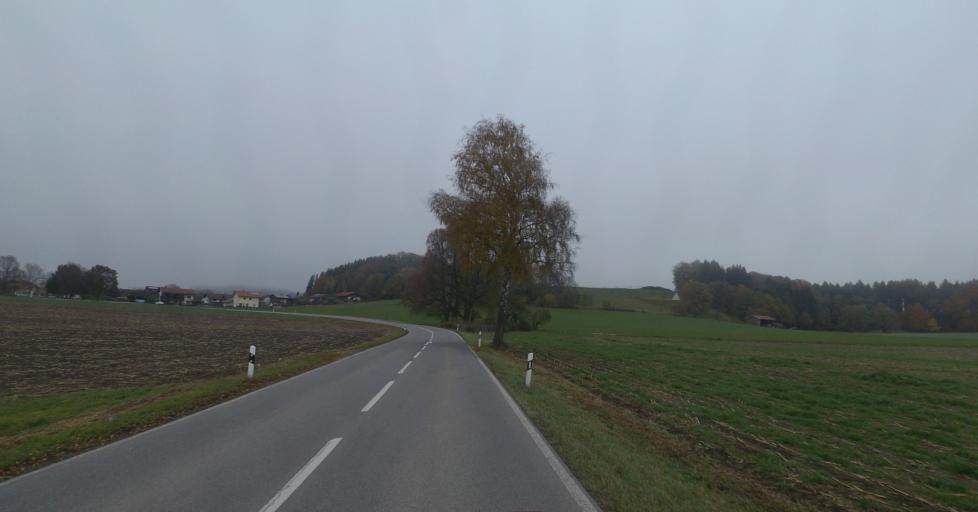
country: DE
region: Bavaria
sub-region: Upper Bavaria
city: Seeon-Seebruck
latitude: 47.9530
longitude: 12.5036
